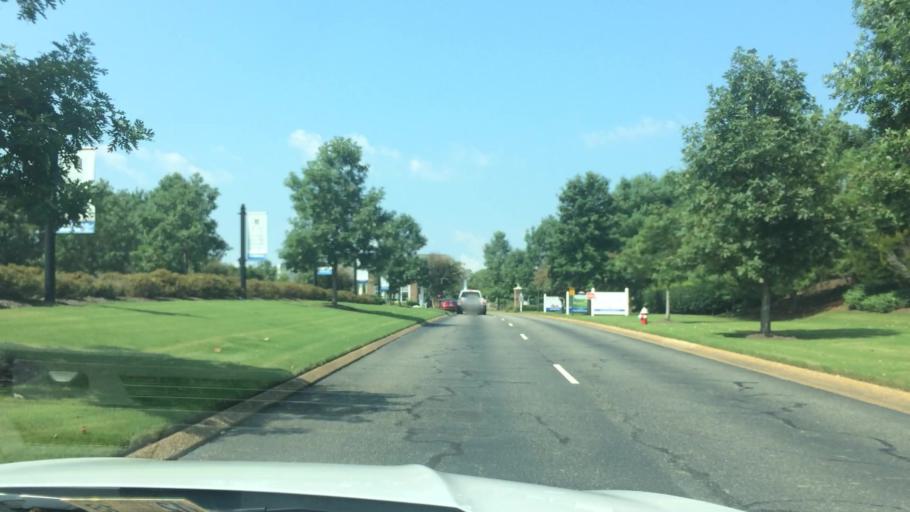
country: US
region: Virginia
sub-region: James City County
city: Williamsburg
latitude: 37.3527
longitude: -76.7653
